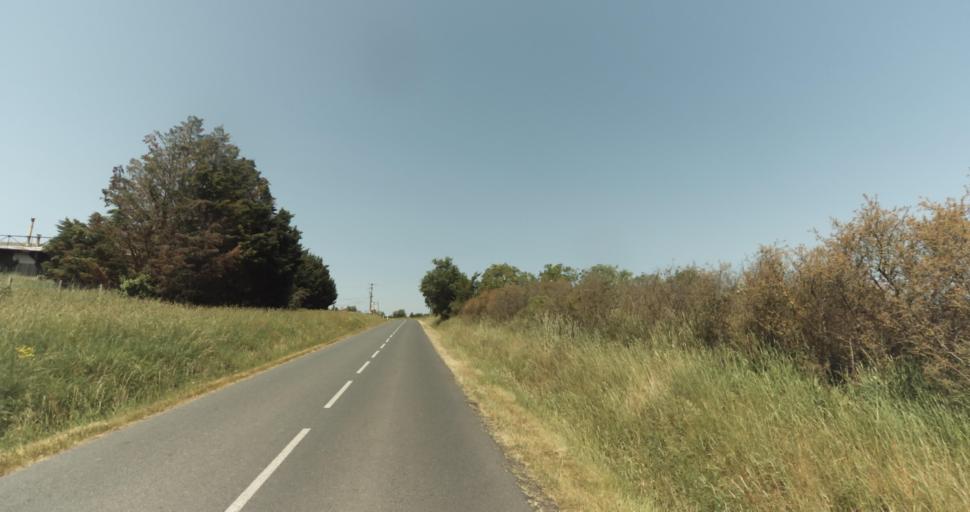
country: FR
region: Midi-Pyrenees
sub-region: Departement de la Haute-Garonne
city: Leguevin
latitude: 43.5755
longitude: 1.2387
